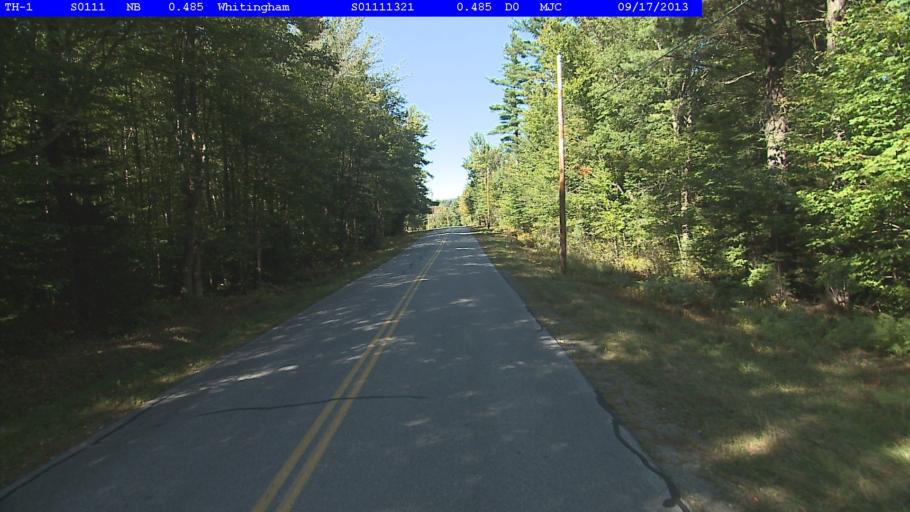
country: US
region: Massachusetts
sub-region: Franklin County
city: Charlemont
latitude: 42.7437
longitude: -72.8161
